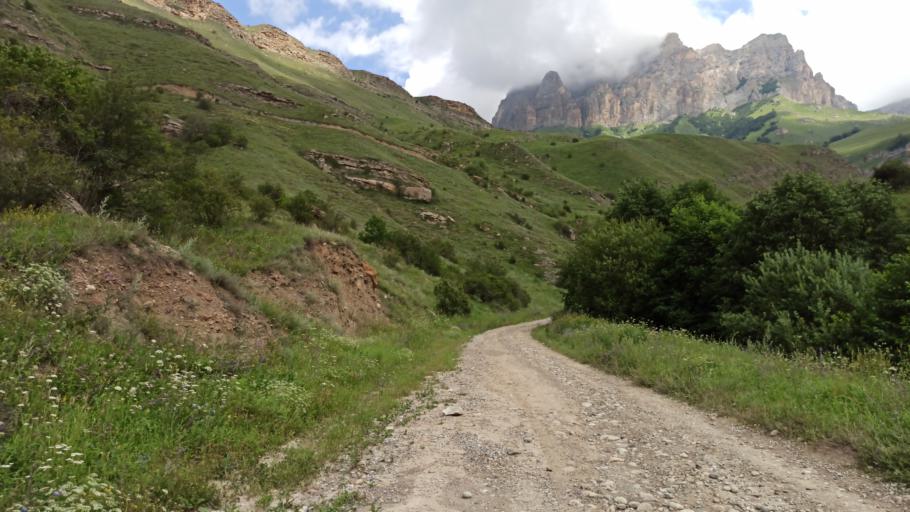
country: RU
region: Kabardino-Balkariya
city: Bylym
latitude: 43.4249
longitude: 43.0466
